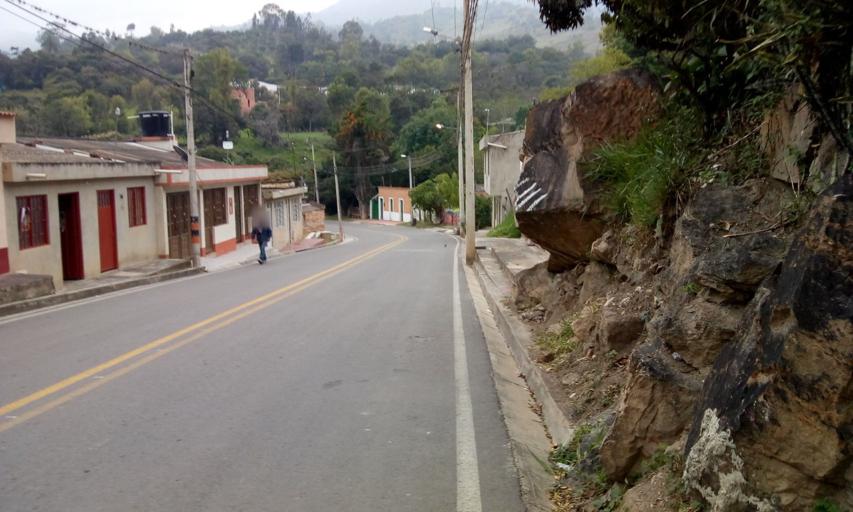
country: CO
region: Boyaca
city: Tipacoque
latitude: 6.4183
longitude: -72.6927
